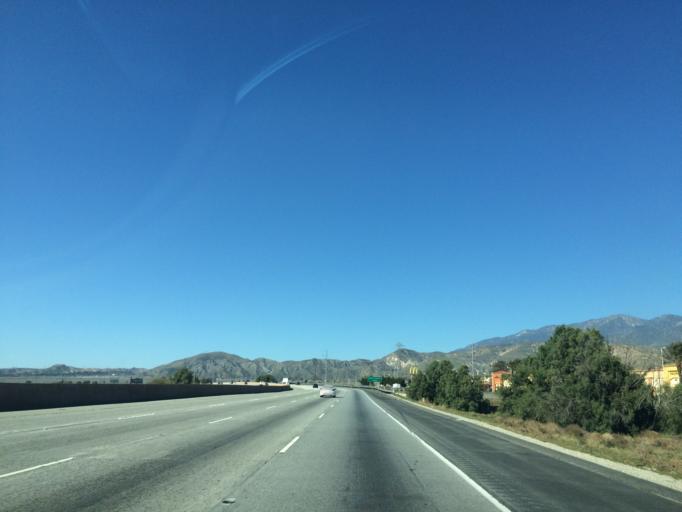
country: US
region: California
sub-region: Riverside County
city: Cabazon
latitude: 33.9285
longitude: -116.8168
